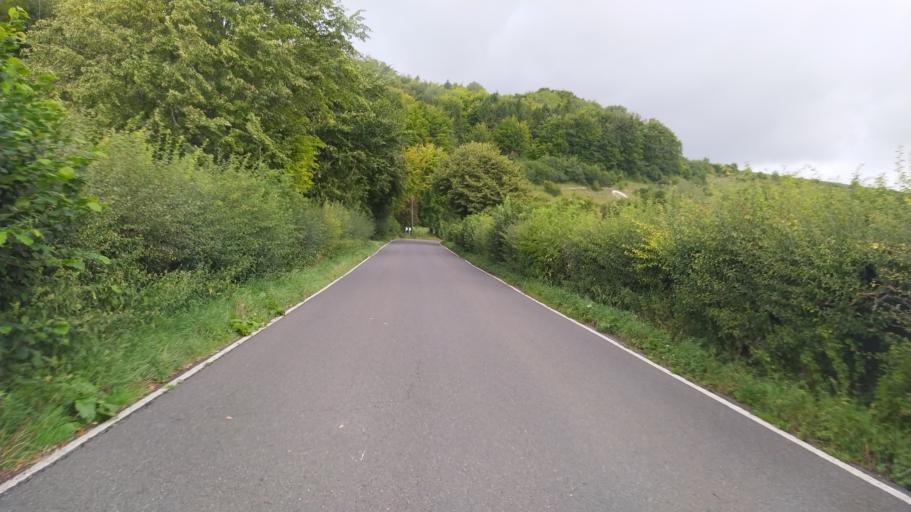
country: GB
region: England
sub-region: Hampshire
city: Cowplain
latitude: 50.9984
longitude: -1.0429
